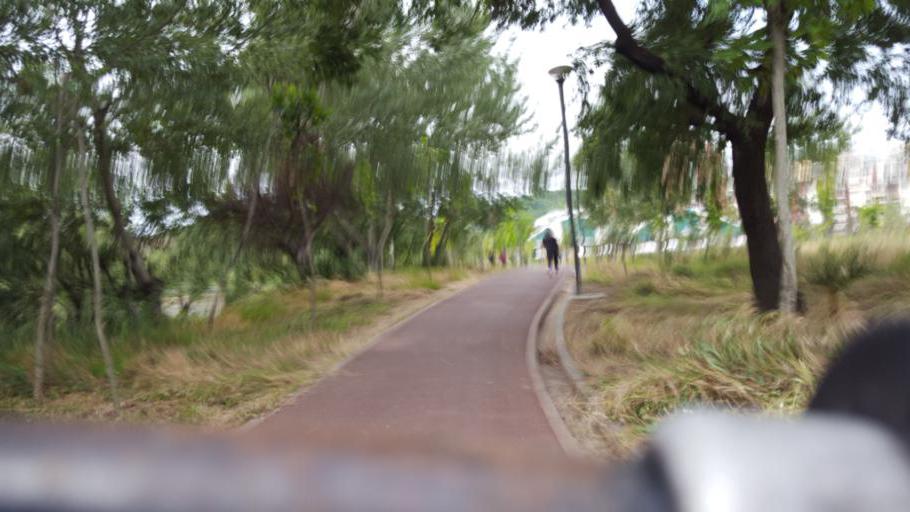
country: AL
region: Tirane
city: Tirana
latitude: 41.3075
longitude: 19.8172
